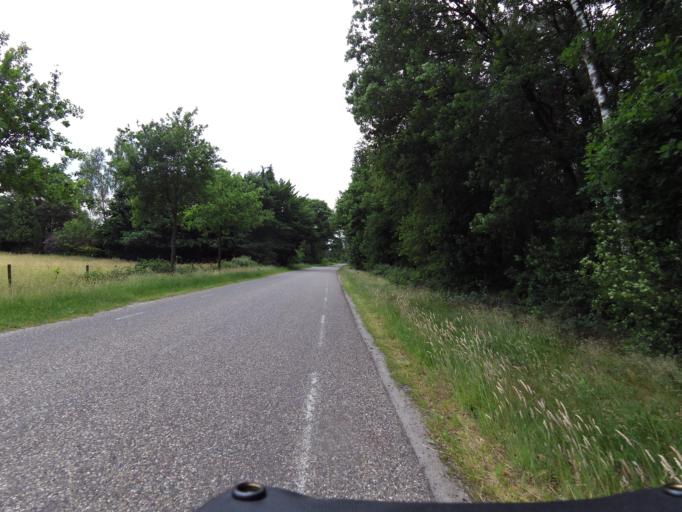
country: NL
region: North Brabant
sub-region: Gemeente Bladel en Netersel
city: Bladel
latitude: 51.4172
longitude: 5.2178
